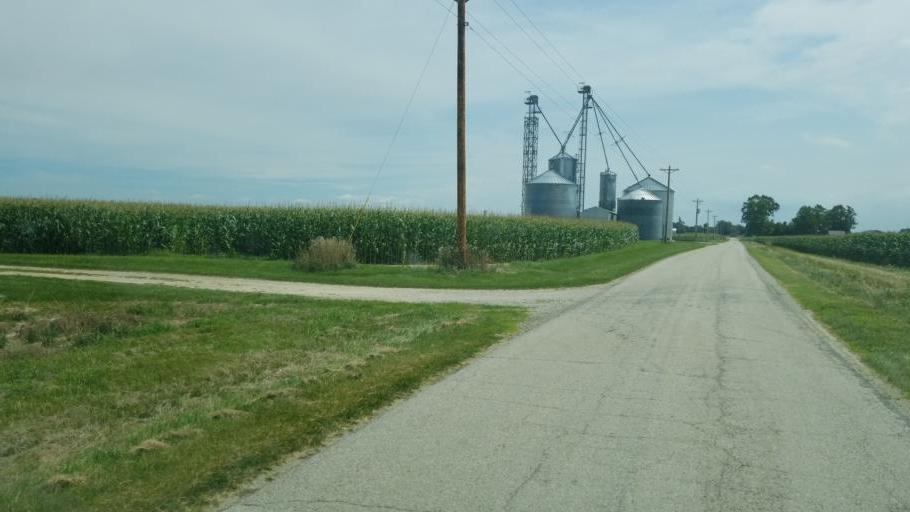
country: US
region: Ohio
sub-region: Crawford County
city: Bucyrus
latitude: 40.8777
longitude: -83.0362
